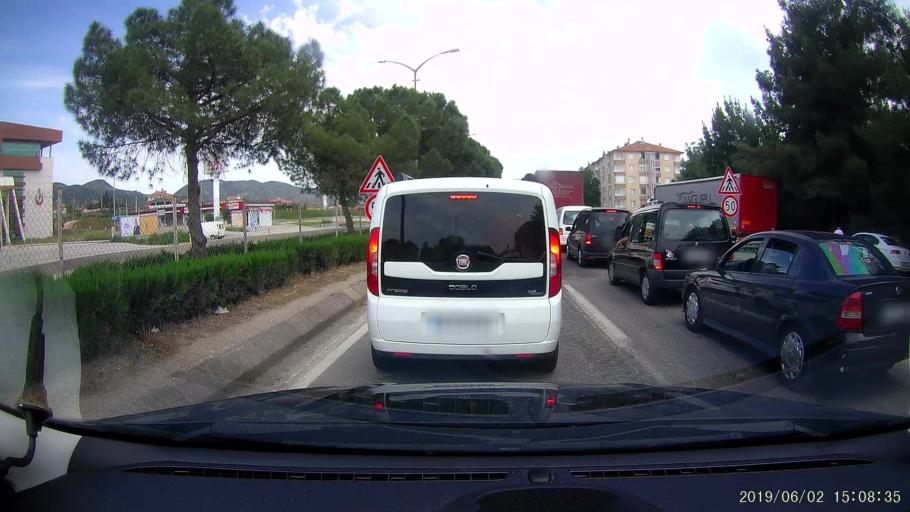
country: TR
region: Corum
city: Osmancik
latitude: 40.9792
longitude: 34.8036
